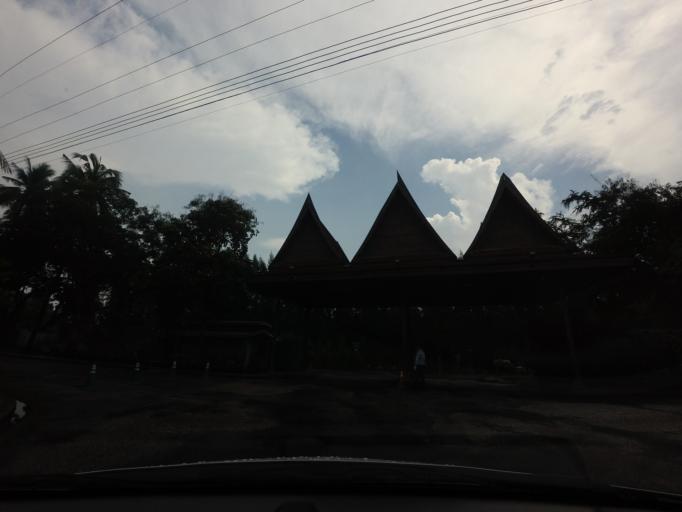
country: TH
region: Nakhon Pathom
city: Sam Phran
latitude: 13.7332
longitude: 100.2440
